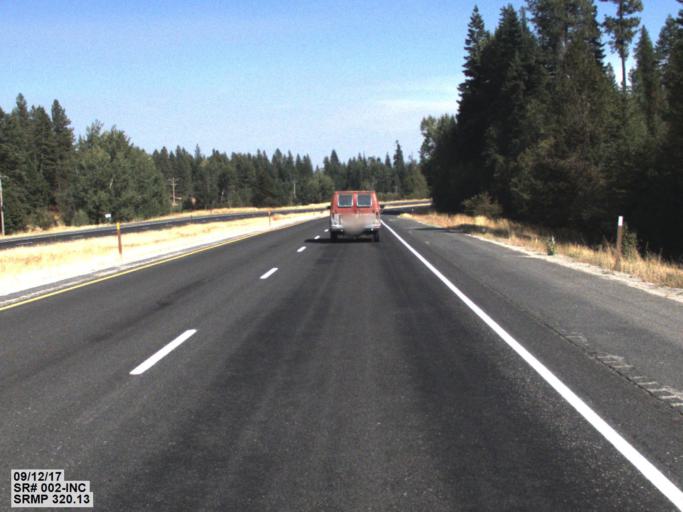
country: US
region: Washington
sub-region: Spokane County
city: Deer Park
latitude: 48.0981
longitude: -117.3029
